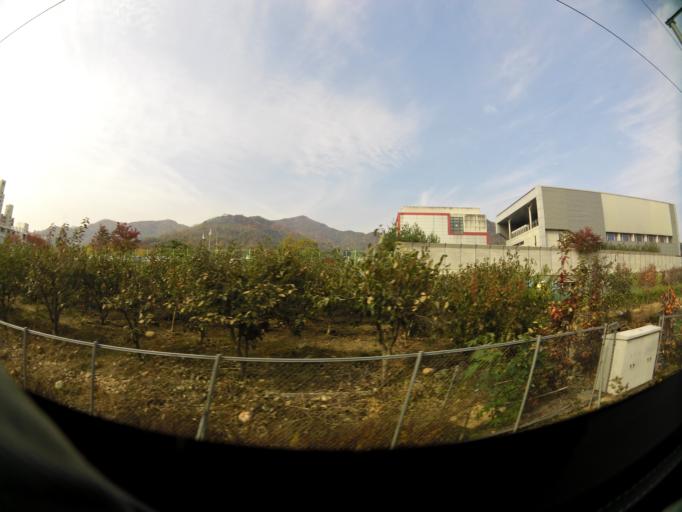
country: KR
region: Gyeongsangbuk-do
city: Gumi
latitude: 36.0900
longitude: 128.3524
